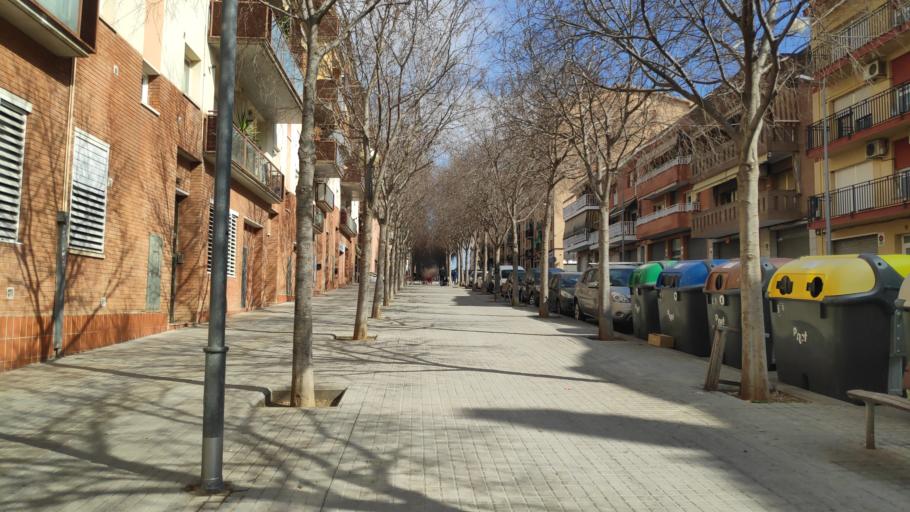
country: ES
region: Catalonia
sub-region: Provincia de Barcelona
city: Sant Quirze del Valles
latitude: 41.5567
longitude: 2.0829
